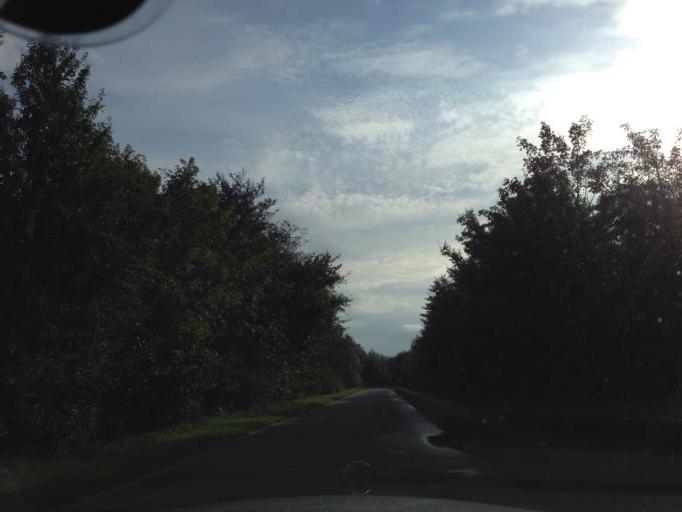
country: DE
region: Schleswig-Holstein
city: Nieblum
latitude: 54.6829
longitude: 8.4915
